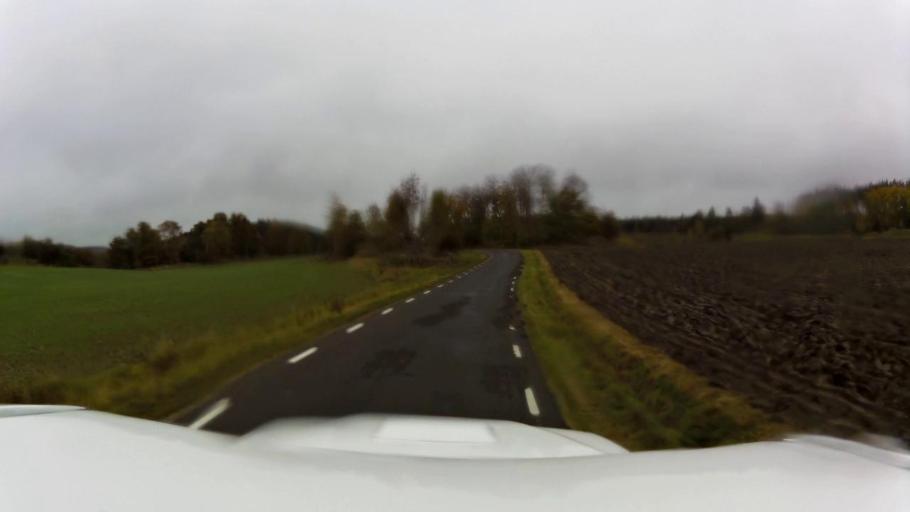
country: SE
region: OEstergoetland
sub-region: Linkopings Kommun
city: Linghem
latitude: 58.3489
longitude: 15.8840
